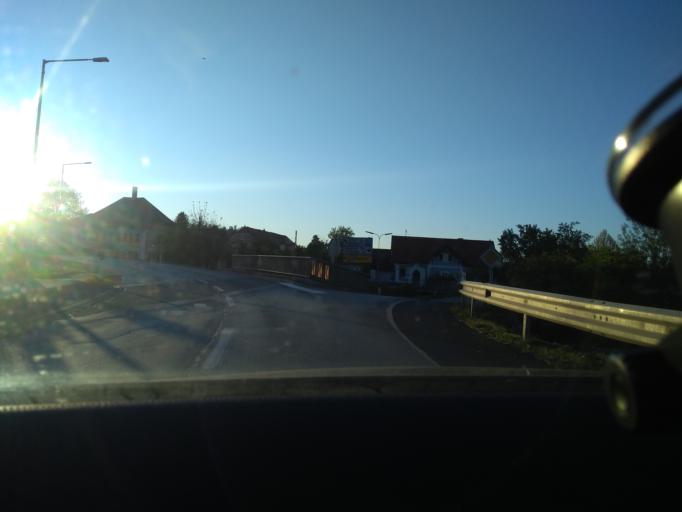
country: AT
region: Styria
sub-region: Politischer Bezirk Voitsberg
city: Mooskirchen
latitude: 46.9997
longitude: 15.2915
